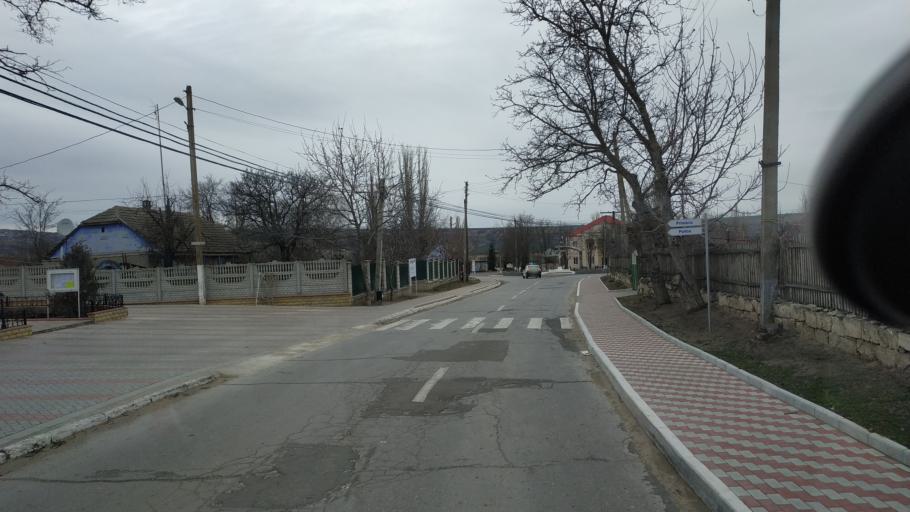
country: MD
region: Telenesti
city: Cocieri
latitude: 47.3456
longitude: 29.0913
